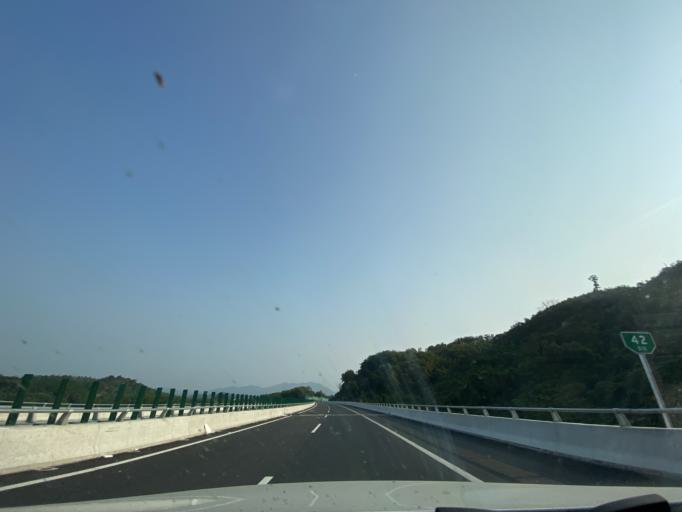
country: CN
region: Hainan
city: Xiangshui
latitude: 18.6527
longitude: 109.6287
